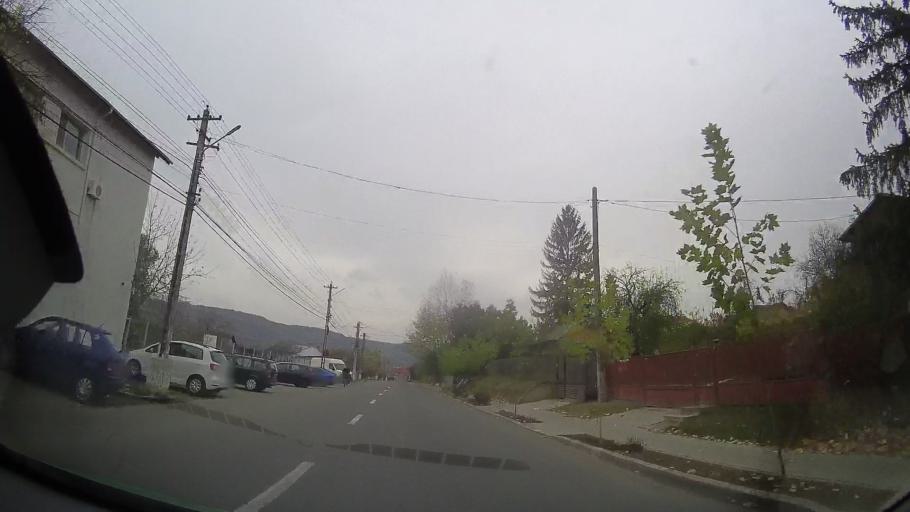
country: RO
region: Prahova
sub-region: Oras Urlati
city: Urlati
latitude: 44.9967
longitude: 26.2298
